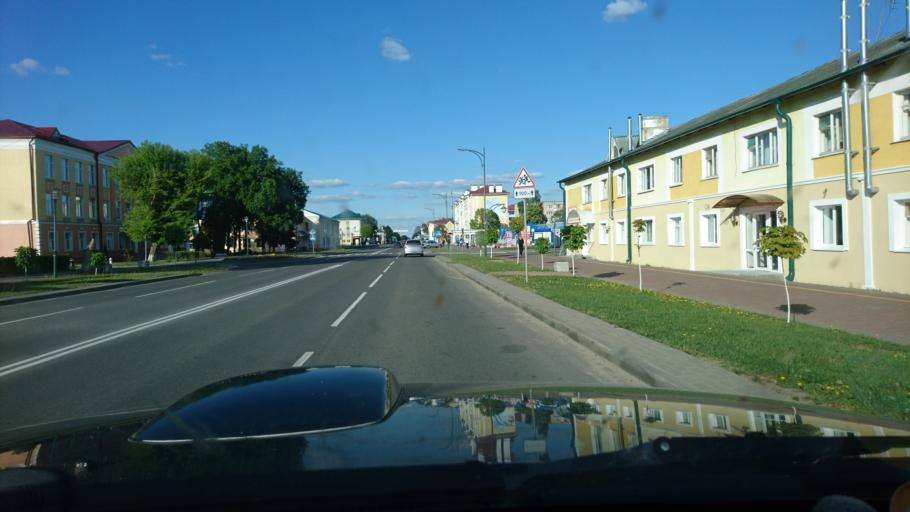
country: BY
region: Brest
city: Byaroza
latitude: 52.5320
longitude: 24.9801
